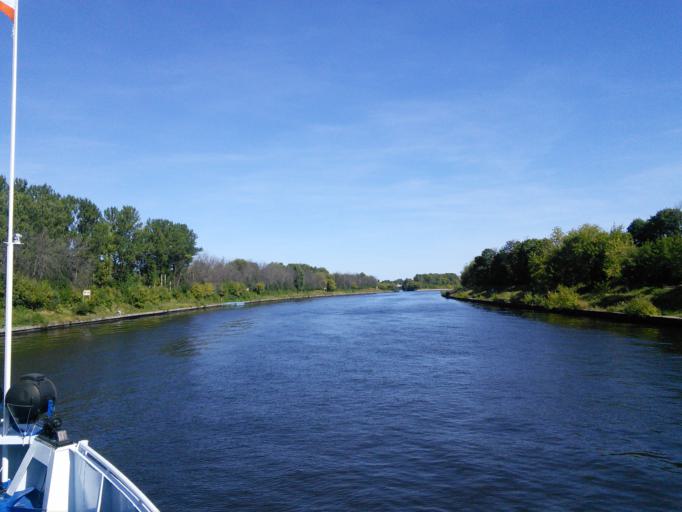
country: RU
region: Moskovskaya
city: Dolgoprudnyy
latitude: 55.9510
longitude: 37.4809
